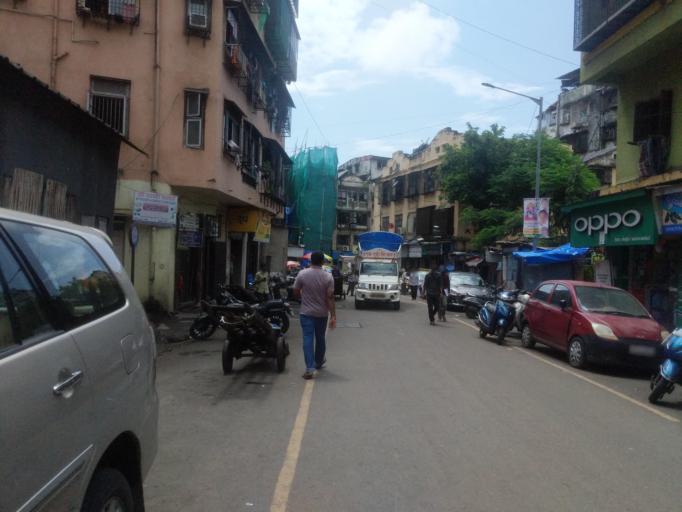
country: IN
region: Maharashtra
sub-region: Raigarh
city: Uran
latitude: 18.9486
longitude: 72.8263
